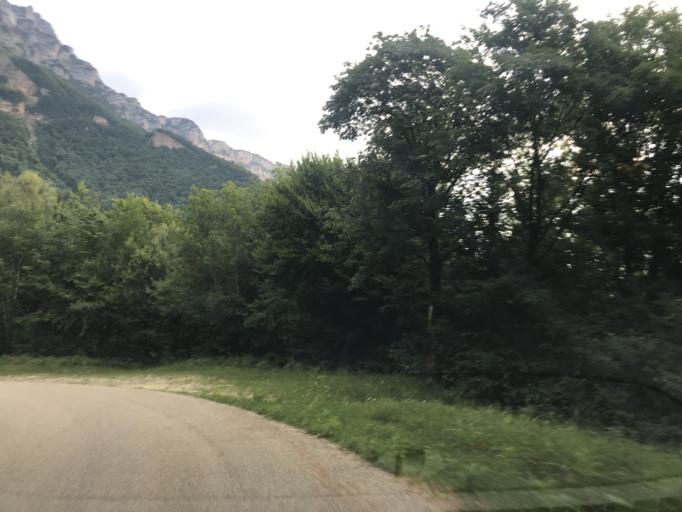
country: FR
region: Rhone-Alpes
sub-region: Departement de l'Isere
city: Saint-Vincent-de-Mercuze
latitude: 45.3731
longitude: 5.9230
